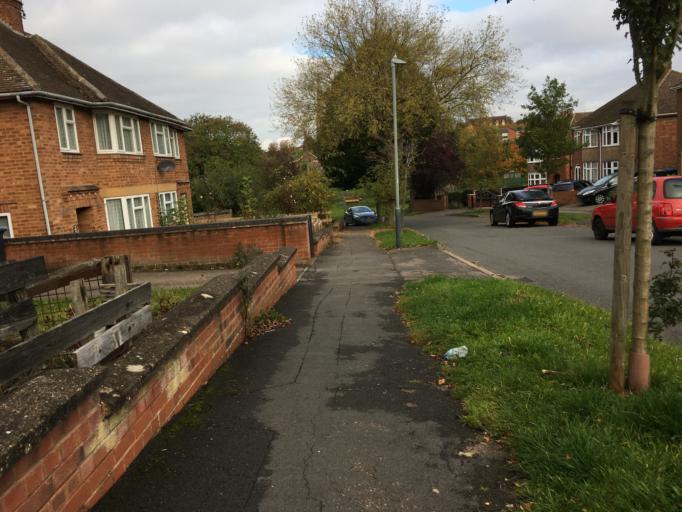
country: GB
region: England
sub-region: Warwickshire
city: Rugby
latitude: 52.3632
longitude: -1.2633
